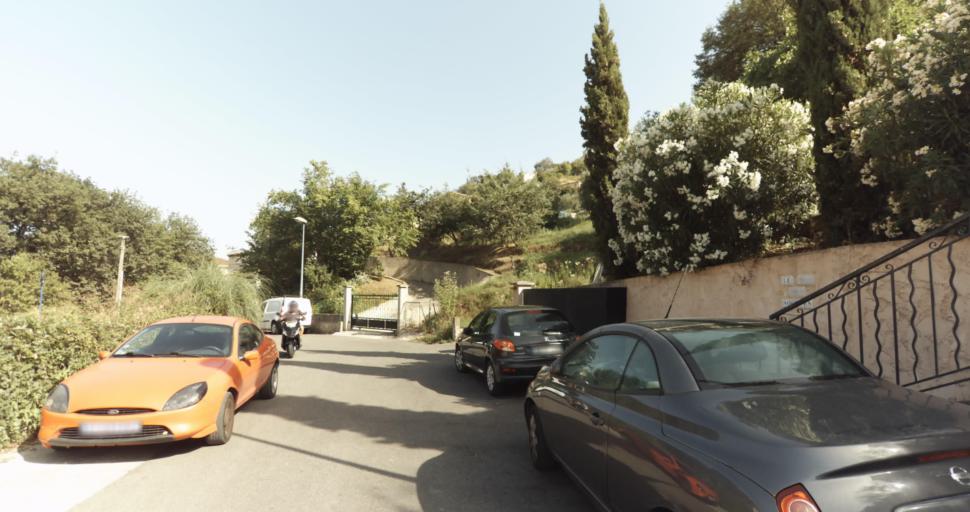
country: FR
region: Provence-Alpes-Cote d'Azur
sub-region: Departement des Alpes-Maritimes
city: Roquebrune-Cap-Martin
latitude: 43.7743
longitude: 7.4855
